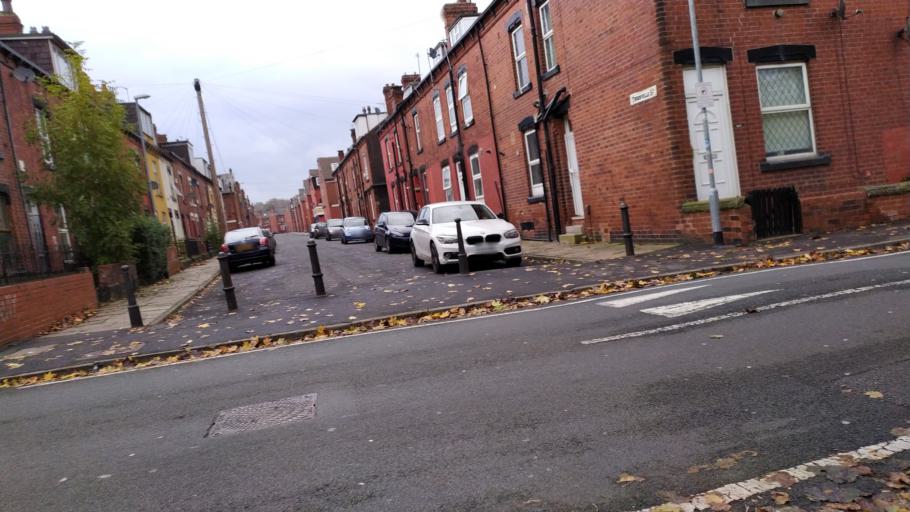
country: GB
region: England
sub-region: City and Borough of Leeds
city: Leeds
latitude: 53.8079
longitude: -1.5725
